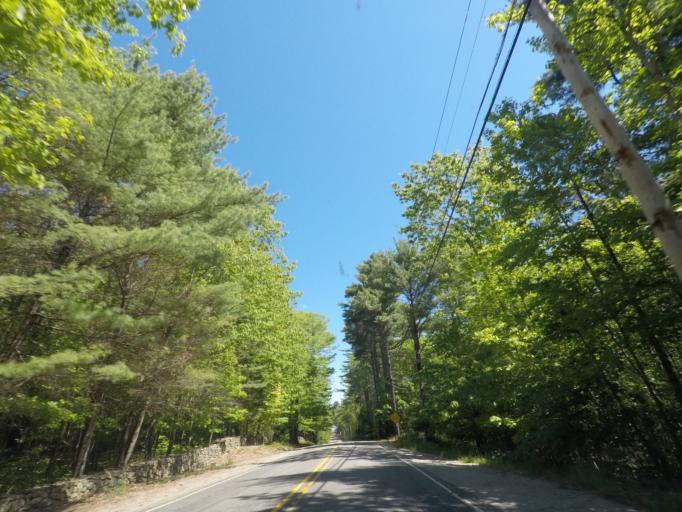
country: US
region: Maine
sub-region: Kennebec County
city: Manchester
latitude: 44.2660
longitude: -69.9023
